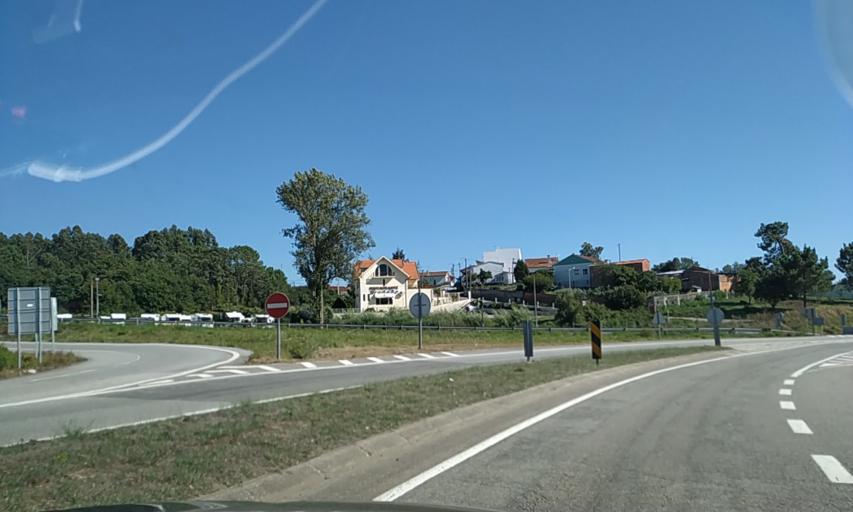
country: PT
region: Aveiro
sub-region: Estarreja
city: Salreu
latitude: 40.6902
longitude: -8.5563
